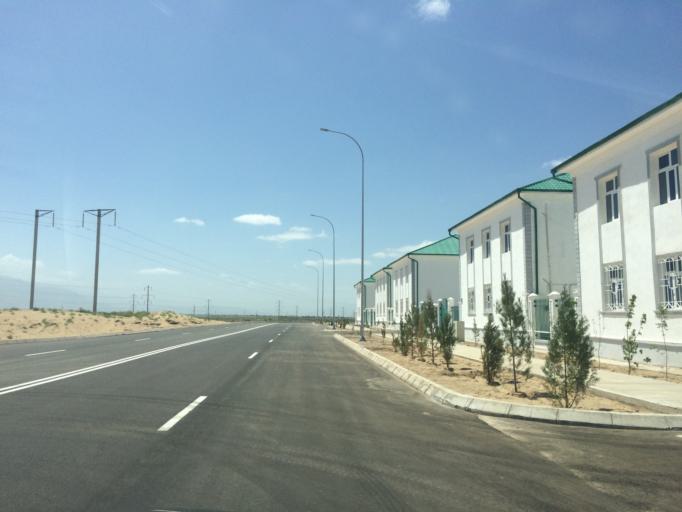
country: TM
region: Ahal
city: Abadan
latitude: 38.0932
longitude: 58.2843
